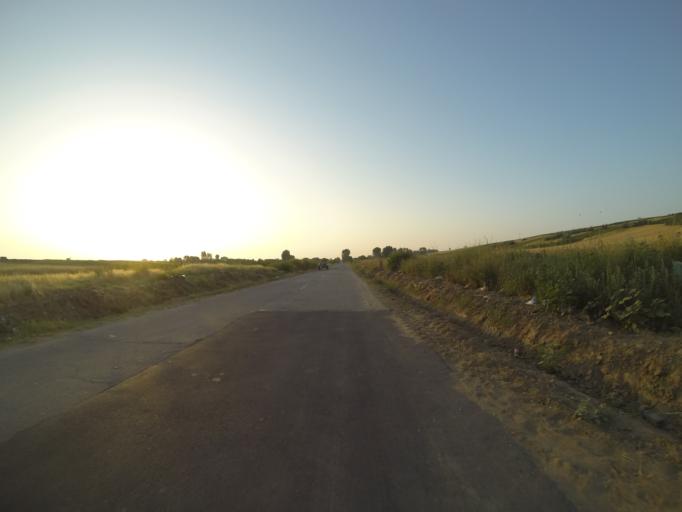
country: RO
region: Dolj
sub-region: Comuna Dobresti
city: Dobresti
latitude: 43.9769
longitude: 23.9793
